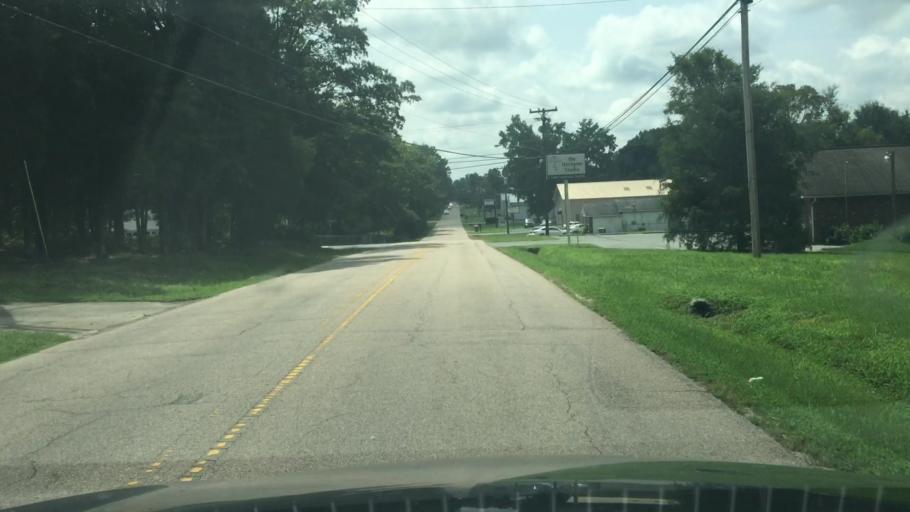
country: US
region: North Carolina
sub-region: Cabarrus County
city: Kannapolis
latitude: 35.4725
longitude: -80.6220
